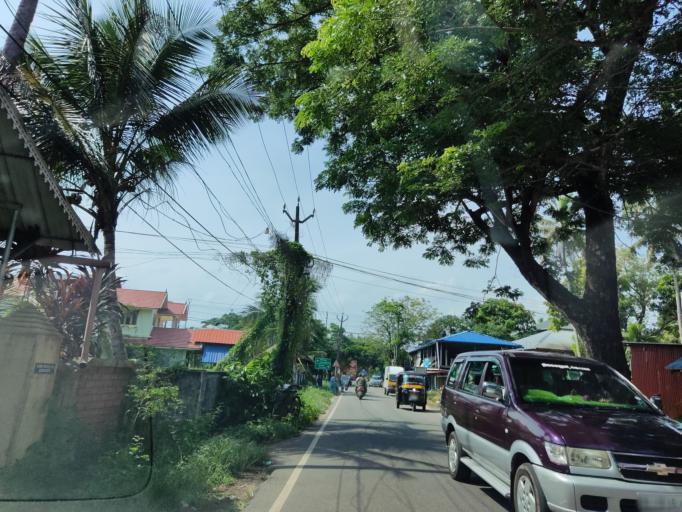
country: IN
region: Kerala
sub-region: Kottayam
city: Changanacheri
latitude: 9.3608
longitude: 76.4688
